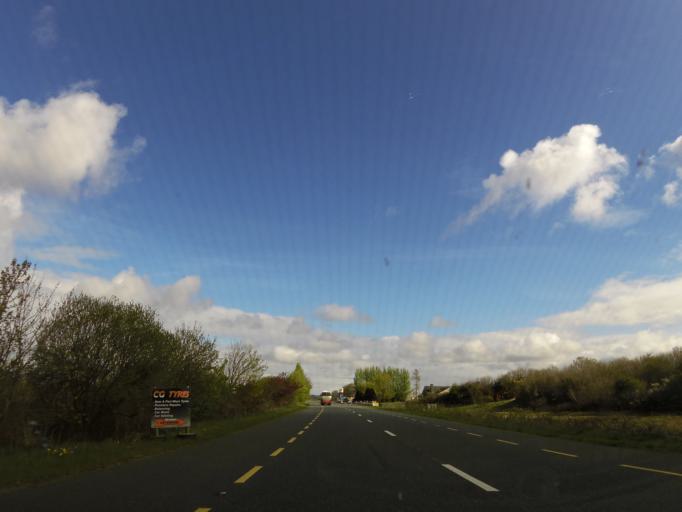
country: IE
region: Connaught
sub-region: Maigh Eo
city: Ballyhaunis
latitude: 53.8490
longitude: -8.8580
